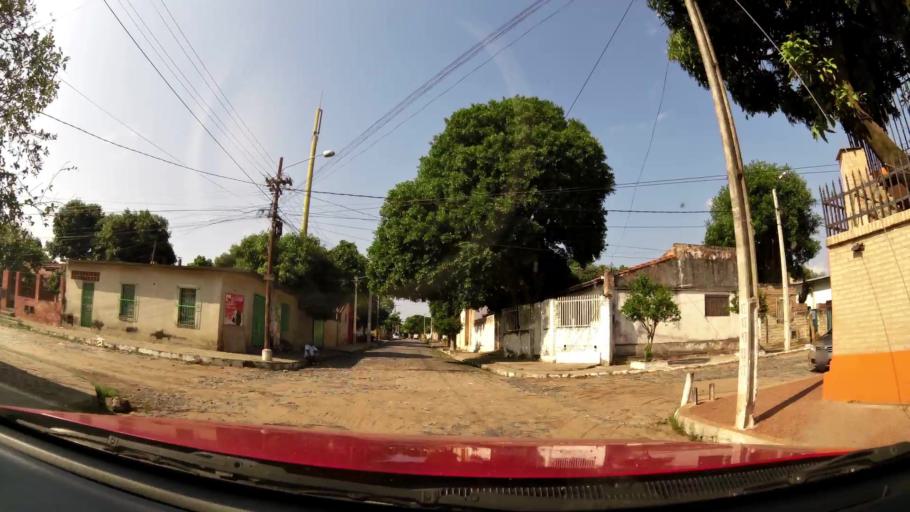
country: PY
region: Asuncion
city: Asuncion
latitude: -25.3191
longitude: -57.6386
